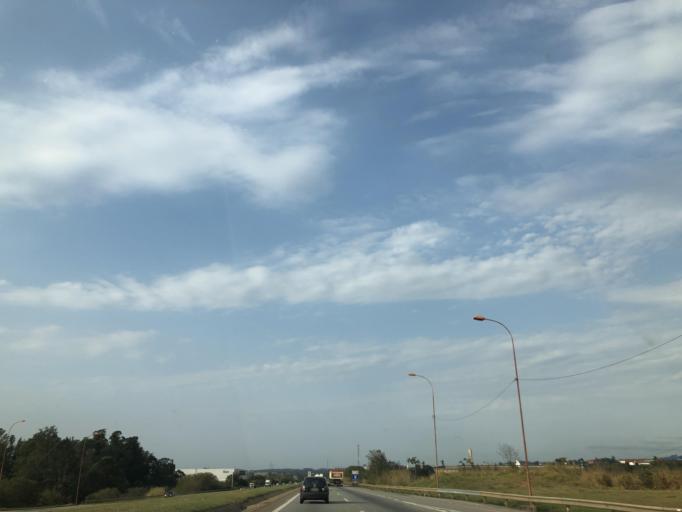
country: BR
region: Sao Paulo
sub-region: Sorocaba
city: Sorocaba
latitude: -23.4344
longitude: -47.3717
